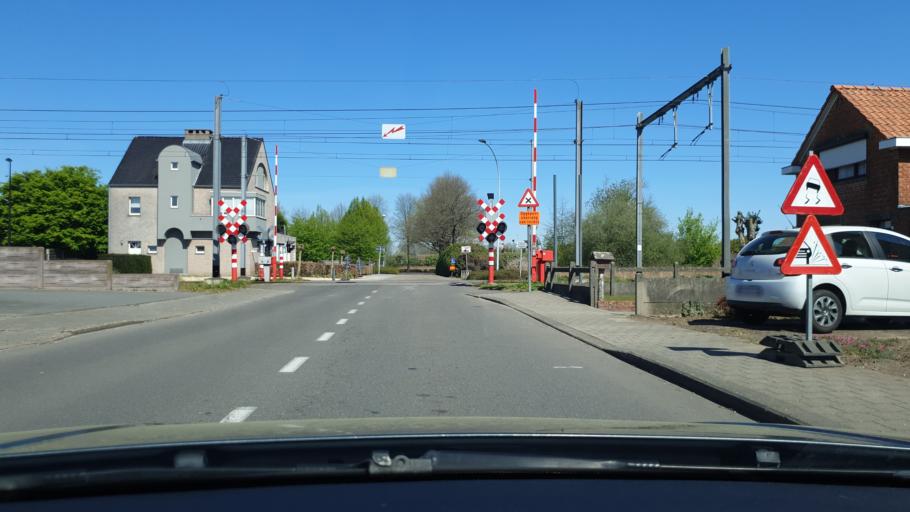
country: BE
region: Flanders
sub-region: Provincie Antwerpen
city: Geel
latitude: 51.1676
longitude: 4.9704
